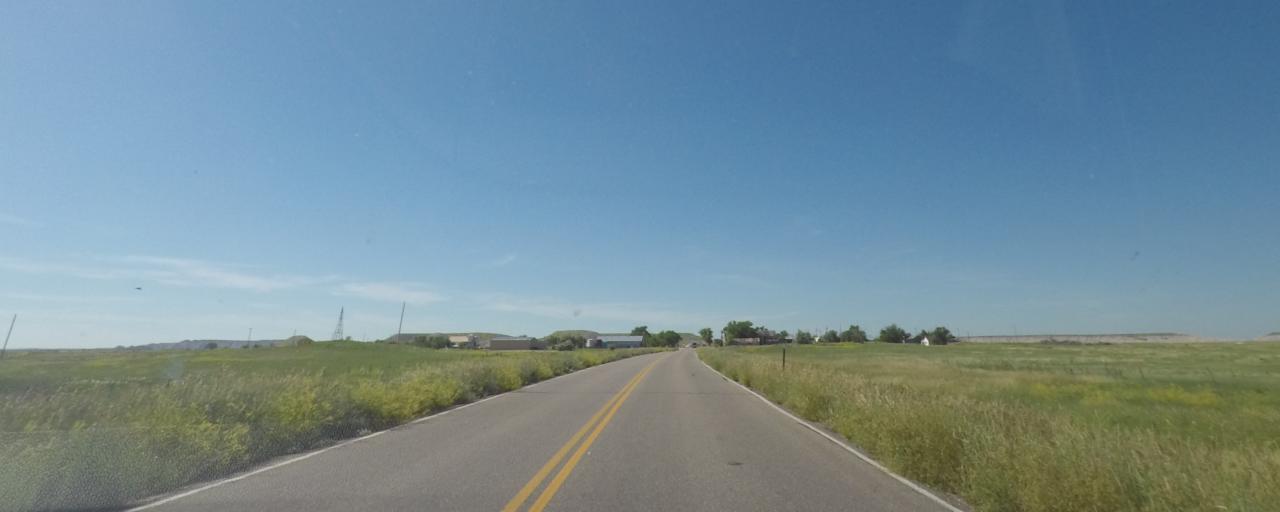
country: US
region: South Dakota
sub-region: Shannon County
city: Porcupine
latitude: 43.7833
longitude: -102.5549
